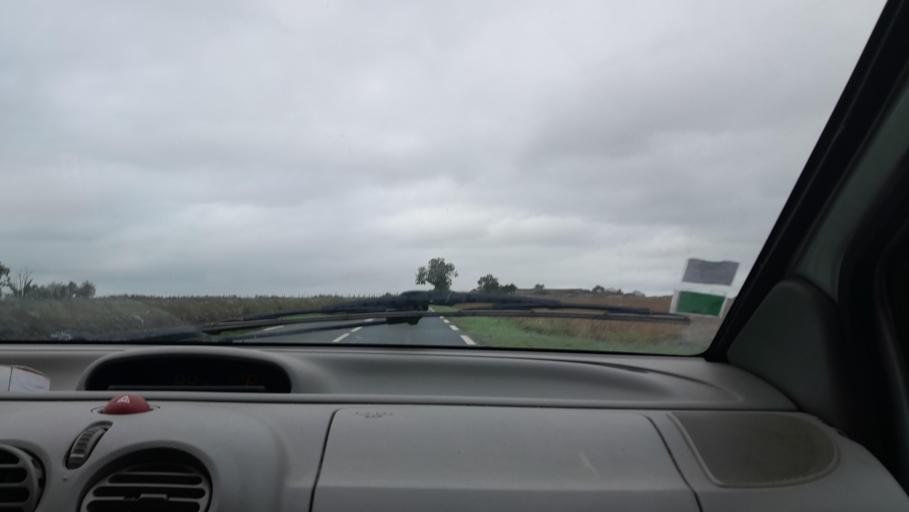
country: FR
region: Pays de la Loire
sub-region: Departement de la Loire-Atlantique
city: Saint-Mars-la-Jaille
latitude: 47.5498
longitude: -1.1857
